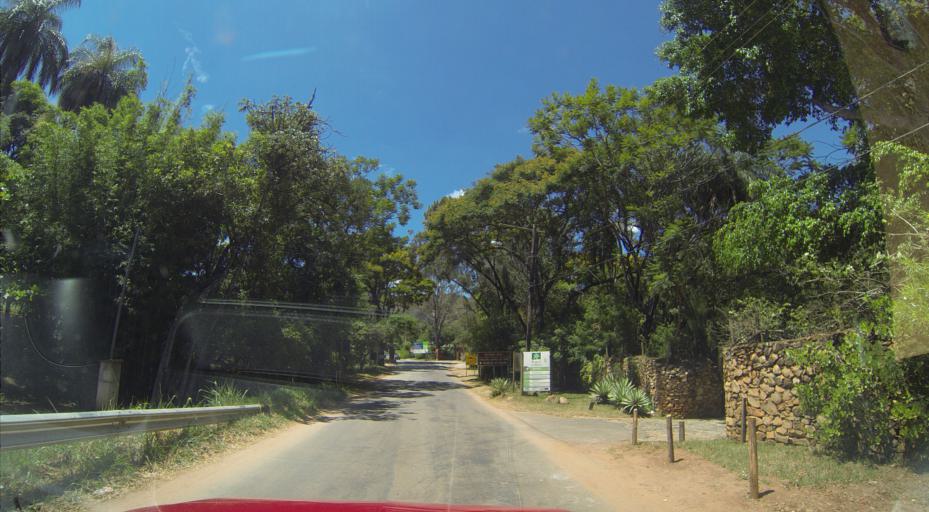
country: BR
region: Minas Gerais
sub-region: Conceicao Do Mato Dentro
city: Conceicao do Mato Dentro
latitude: -19.3182
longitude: -43.6086
